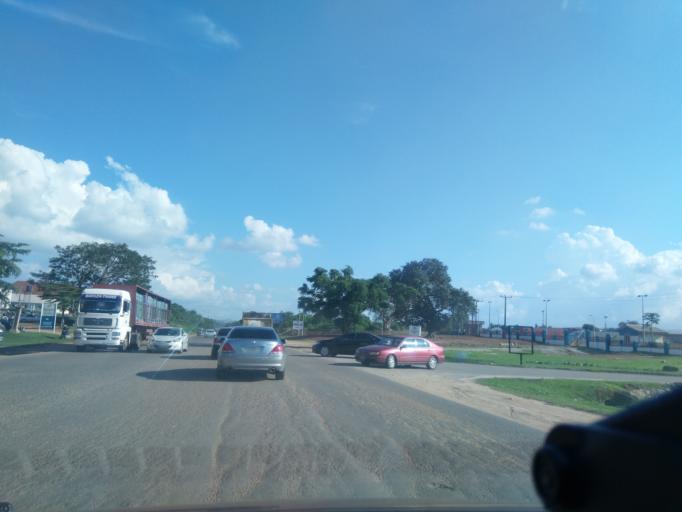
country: NG
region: Abuja Federal Capital Territory
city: Abuja
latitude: 9.0542
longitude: 7.4108
